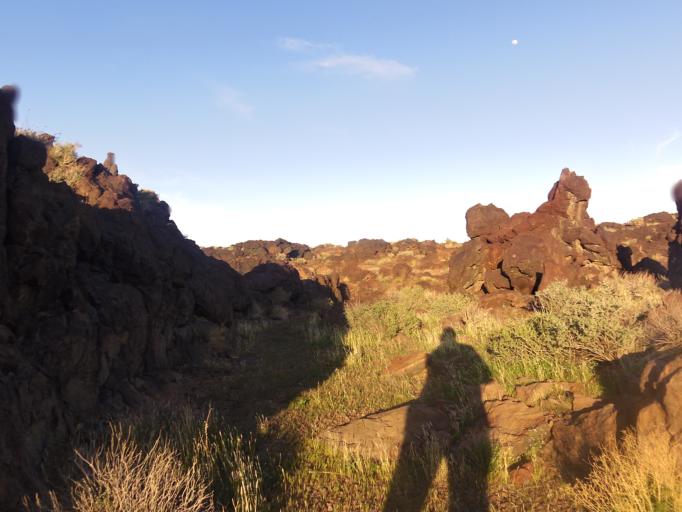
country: US
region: California
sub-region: Kern County
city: Inyokern
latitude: 35.9693
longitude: -117.9089
